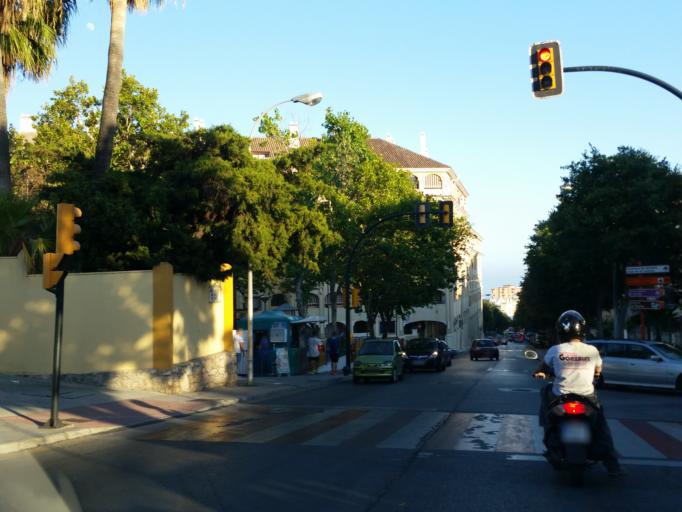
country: ES
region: Andalusia
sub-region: Provincia de Malaga
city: Benalmadena
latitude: 36.6031
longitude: -4.5330
